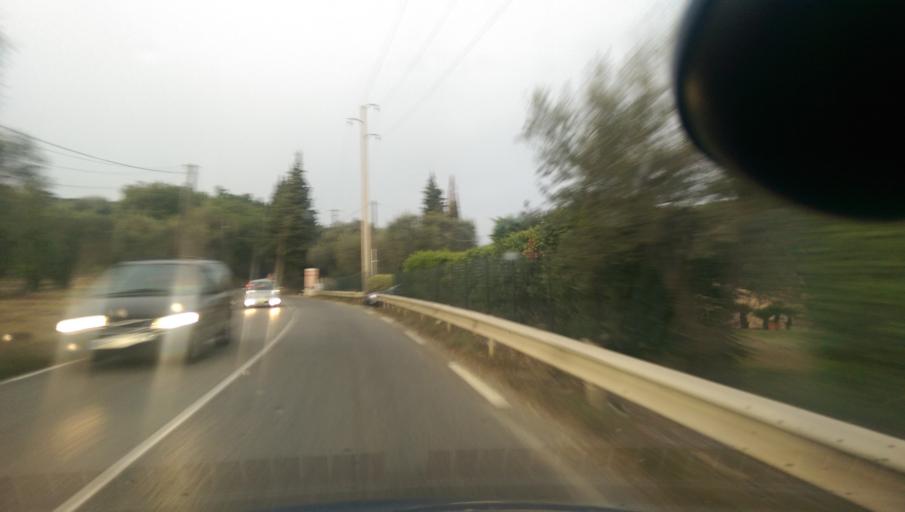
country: FR
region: Provence-Alpes-Cote d'Azur
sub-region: Departement des Alpes-Maritimes
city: Opio
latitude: 43.6718
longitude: 6.9828
